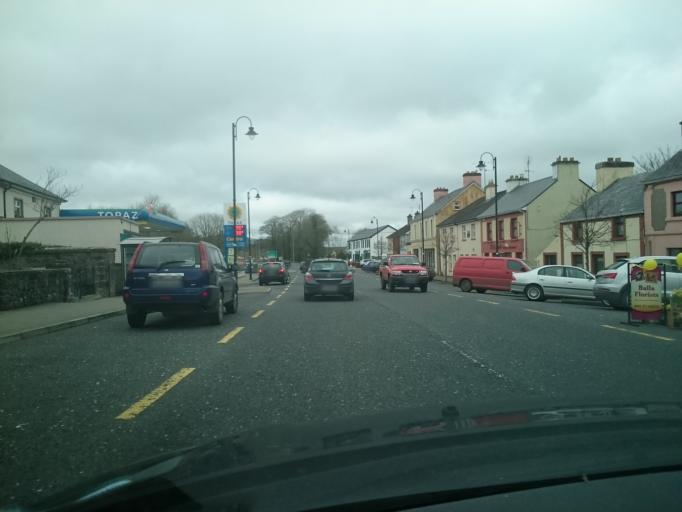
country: IE
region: Connaught
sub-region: Maigh Eo
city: Kiltamagh
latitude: 53.8050
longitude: -9.1306
